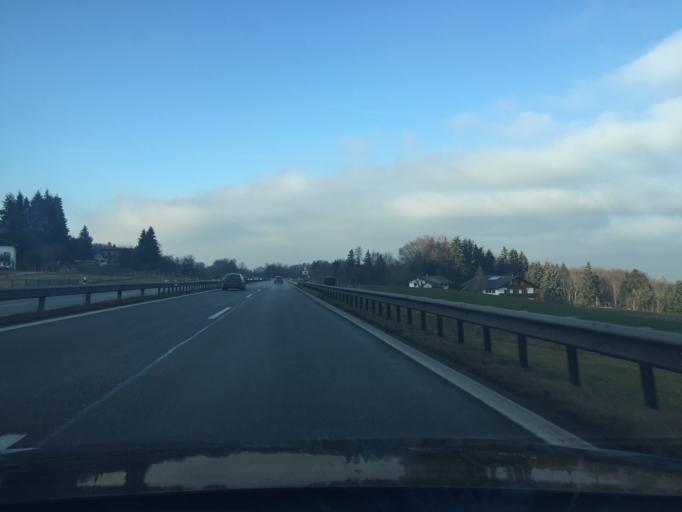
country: DE
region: Bavaria
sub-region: Upper Bavaria
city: Anger
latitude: 47.8160
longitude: 12.8315
